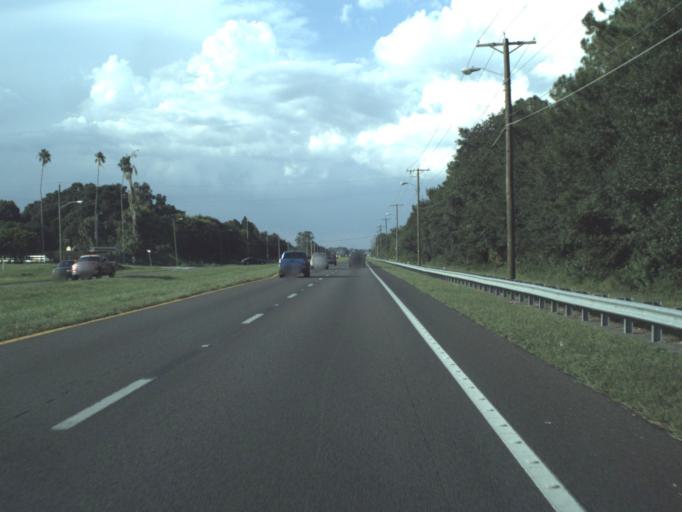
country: US
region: Florida
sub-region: Polk County
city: Mulberry
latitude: 27.9191
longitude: -81.9738
